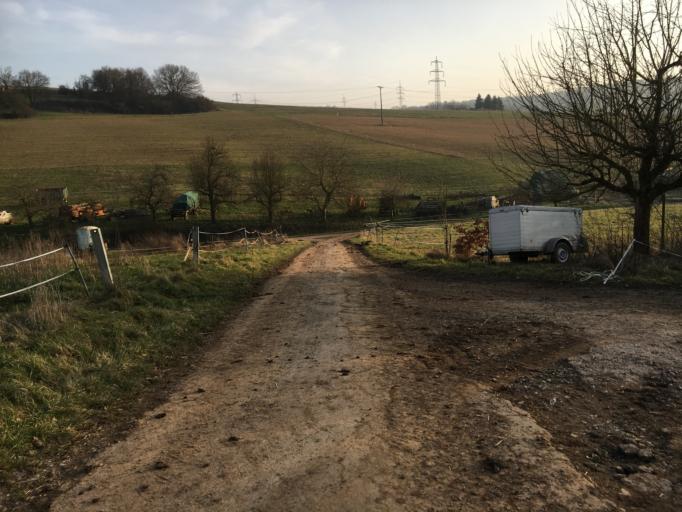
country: DE
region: Baden-Wuerttemberg
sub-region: Karlsruhe Region
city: Huffenhardt
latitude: 49.3203
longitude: 9.0503
